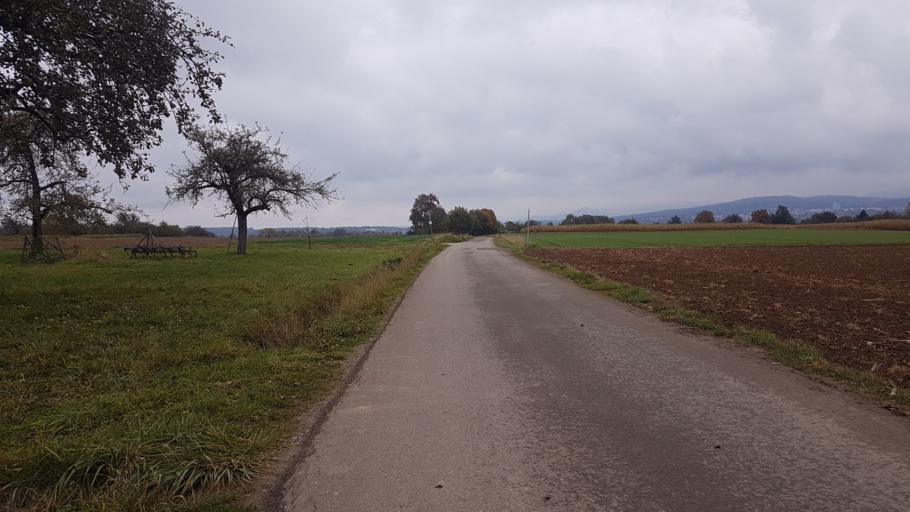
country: DE
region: Baden-Wuerttemberg
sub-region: Tuebingen Region
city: Dusslingen
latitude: 48.4574
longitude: 9.0375
